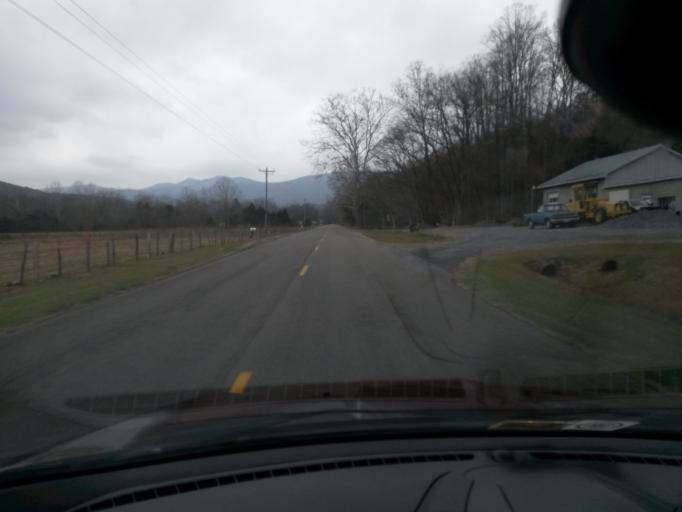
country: US
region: Virginia
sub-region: City of Lexington
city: Lexington
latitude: 37.8655
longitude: -79.5305
